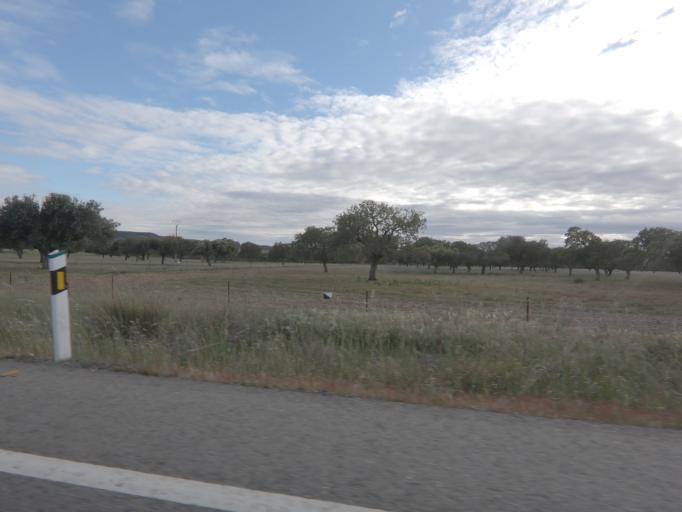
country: ES
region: Extremadura
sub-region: Provincia de Caceres
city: Torrejoncillo
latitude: 39.8700
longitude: -6.4401
